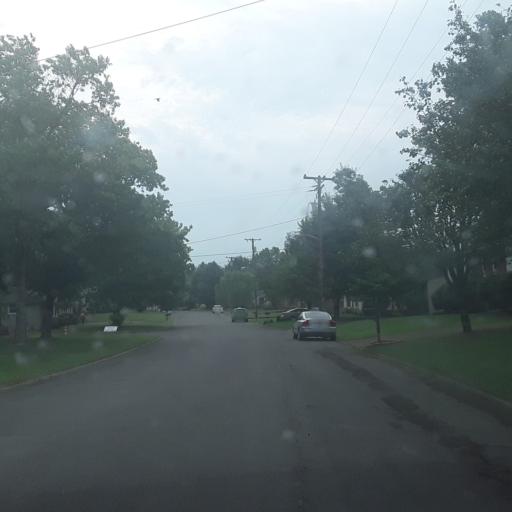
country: US
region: Tennessee
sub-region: Williamson County
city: Brentwood
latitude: 36.0498
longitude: -86.7349
